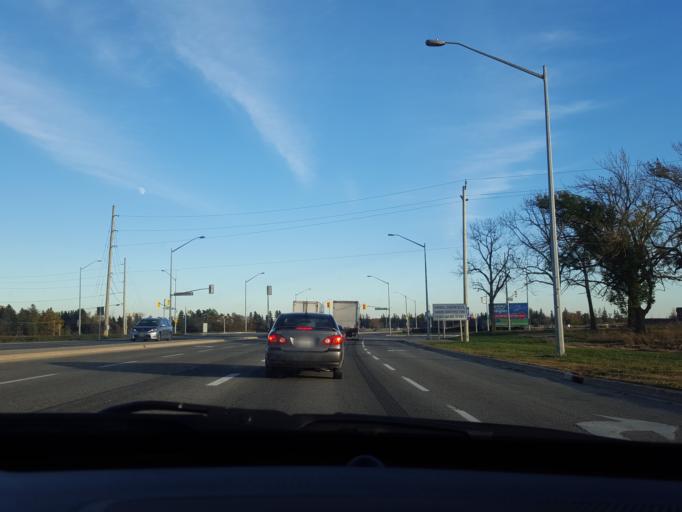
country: CA
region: Ontario
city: Markham
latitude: 43.9014
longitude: -79.2188
